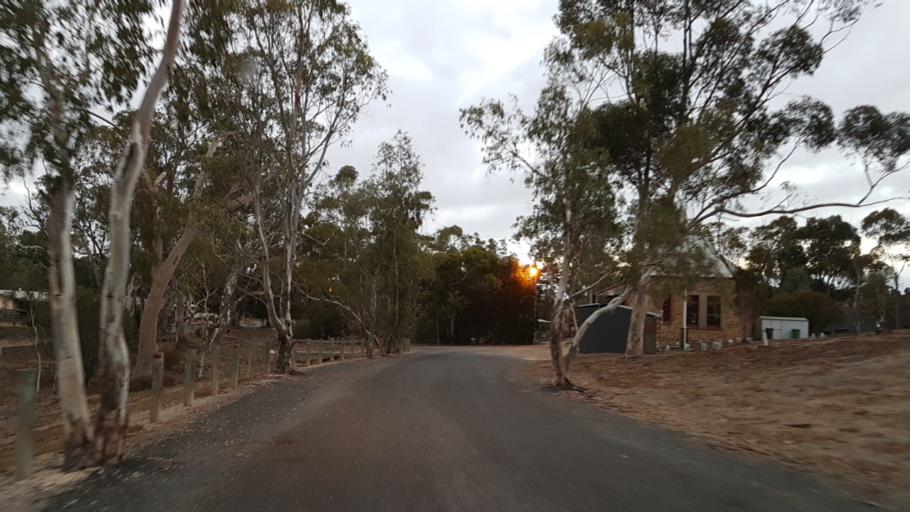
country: AU
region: South Australia
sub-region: Mount Barker
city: Callington
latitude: -35.0695
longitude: 139.0140
